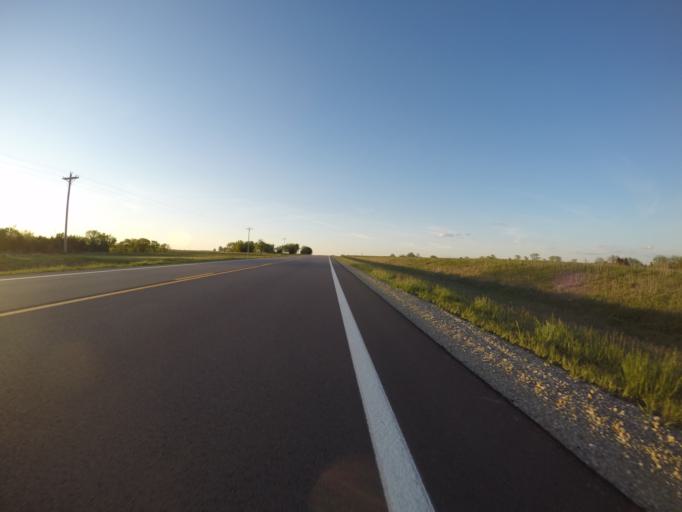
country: US
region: Kansas
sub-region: Pottawatomie County
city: Westmoreland
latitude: 39.3877
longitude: -96.5198
